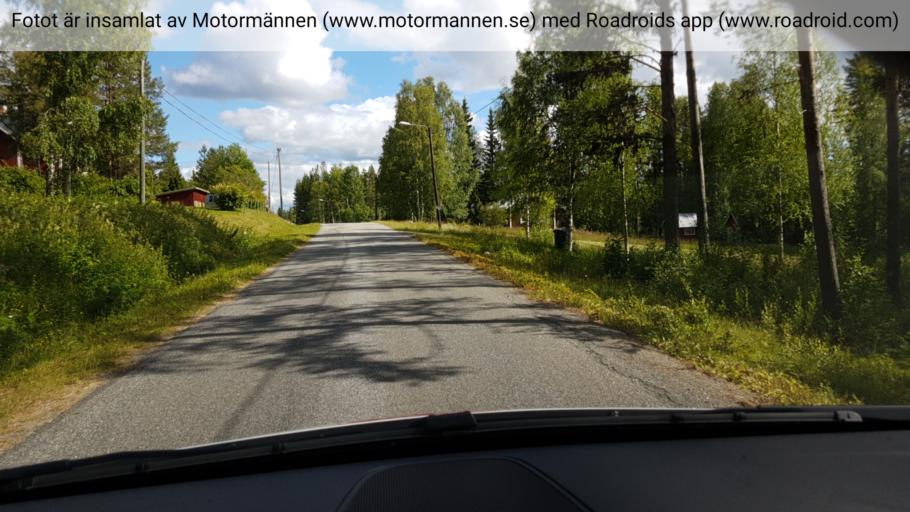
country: SE
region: Vaesterbotten
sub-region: Dorotea Kommun
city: Dorotea
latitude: 64.1020
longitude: 16.3951
